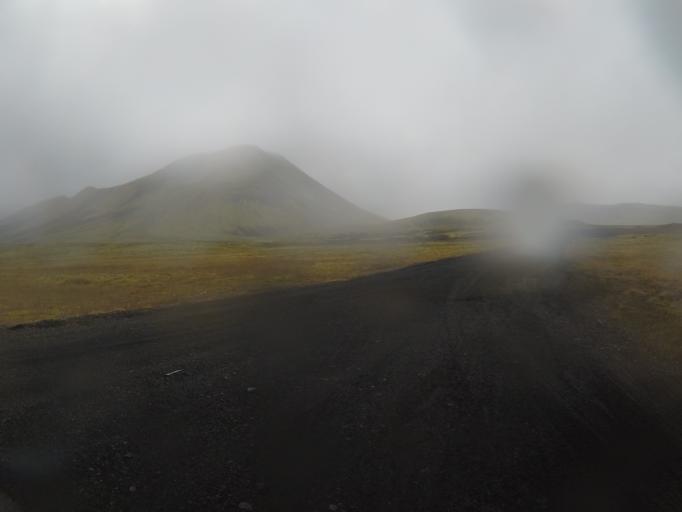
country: IS
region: South
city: Vestmannaeyjar
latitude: 63.9712
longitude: -18.8265
